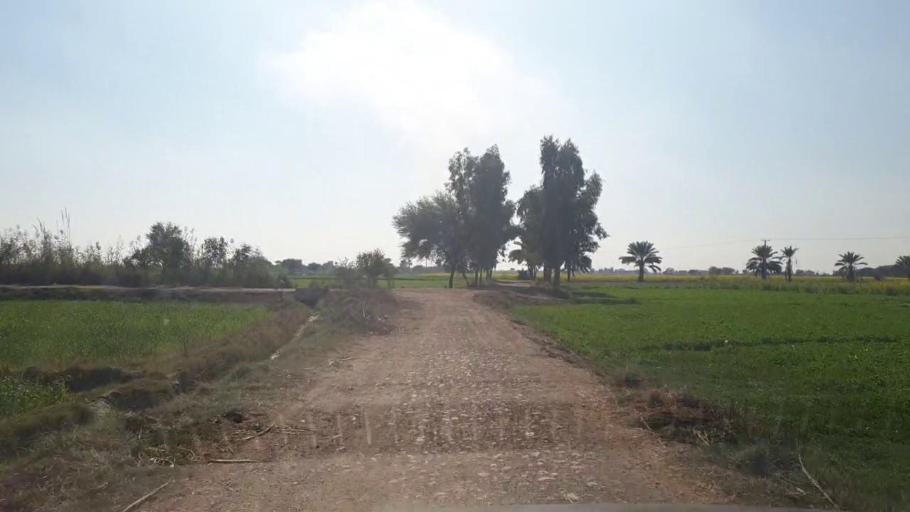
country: PK
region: Sindh
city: Shahdadpur
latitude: 25.9163
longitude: 68.5831
